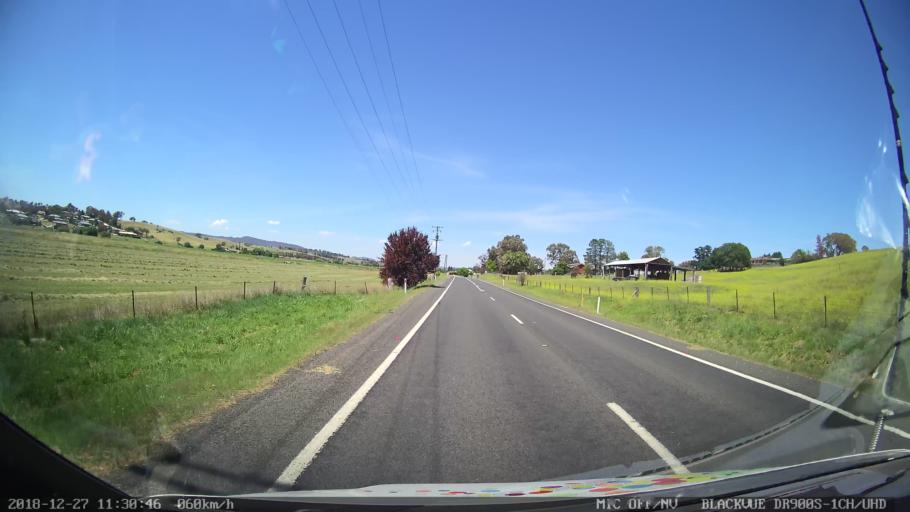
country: AU
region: New South Wales
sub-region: Bathurst Regional
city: Perthville
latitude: -33.4889
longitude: 149.5429
